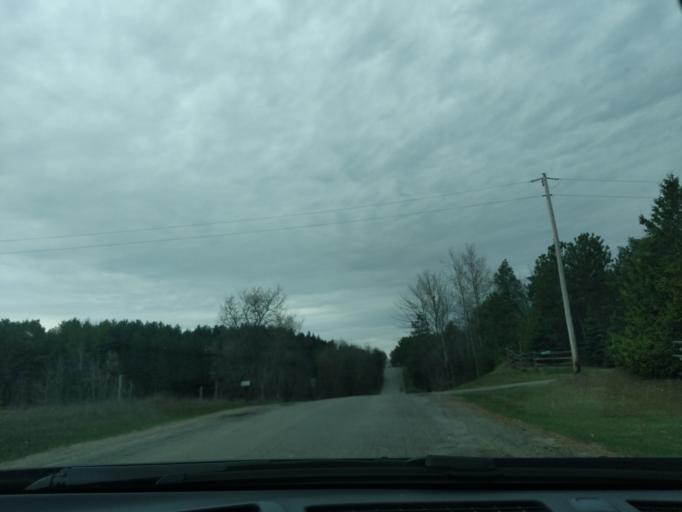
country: CA
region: Ontario
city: Orangeville
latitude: 44.0066
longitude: -79.9653
